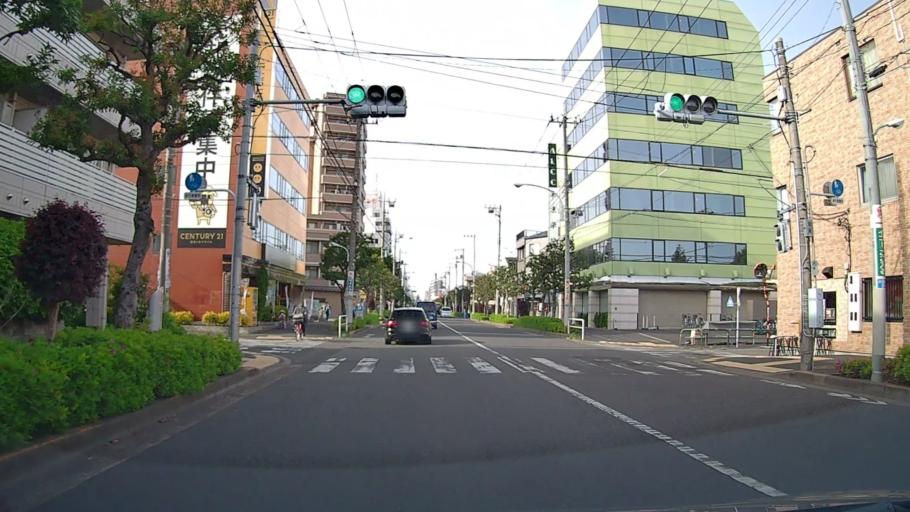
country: JP
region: Saitama
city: Soka
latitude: 35.7927
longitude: 139.7874
